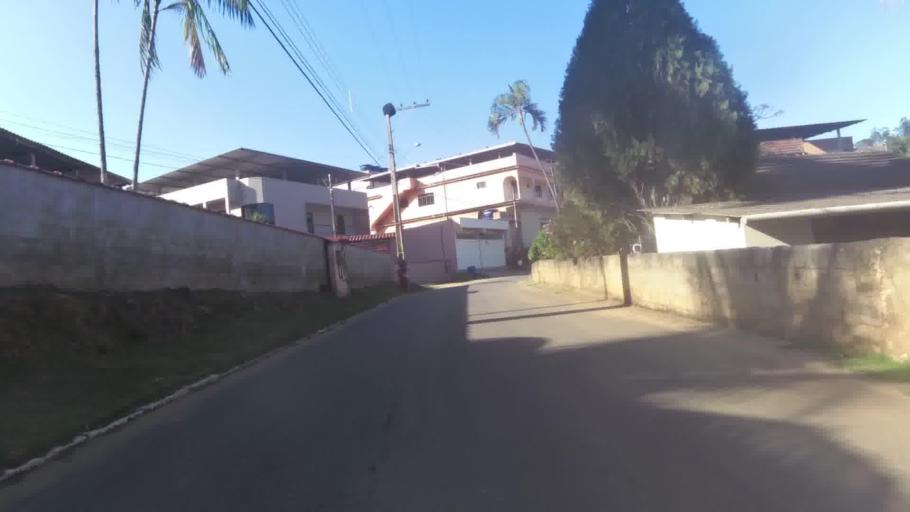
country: BR
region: Espirito Santo
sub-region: Iconha
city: Iconha
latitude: -20.7298
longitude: -40.7788
